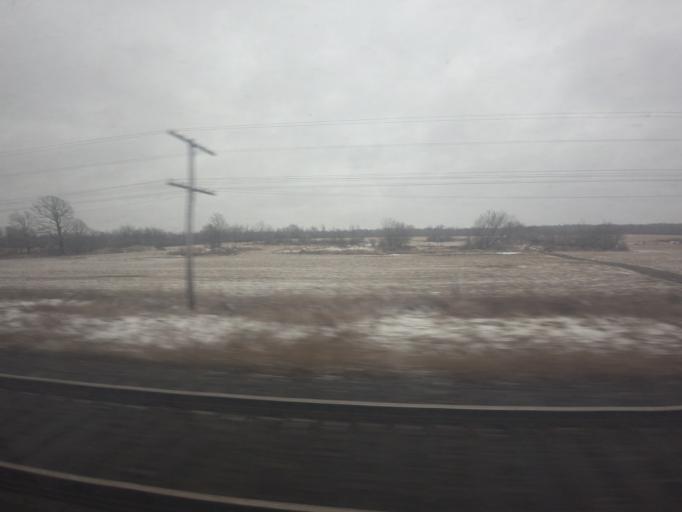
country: CA
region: Ontario
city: Gananoque
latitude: 44.3482
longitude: -76.2632
